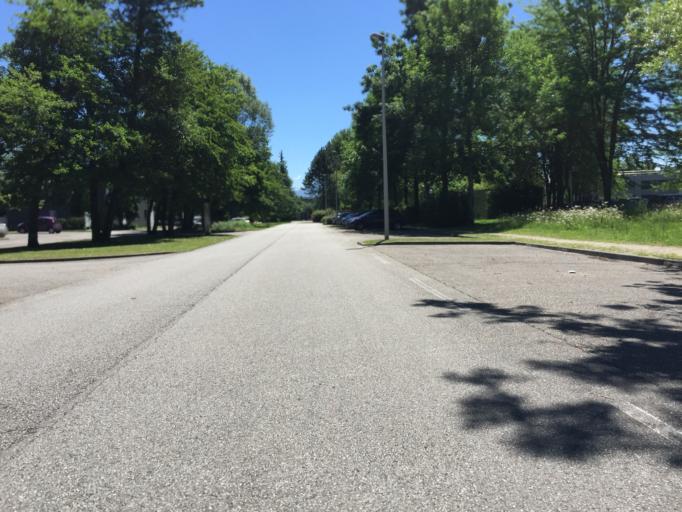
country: FR
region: Rhone-Alpes
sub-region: Departement de la Savoie
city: Le Bourget-du-Lac
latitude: 45.6460
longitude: 5.8674
